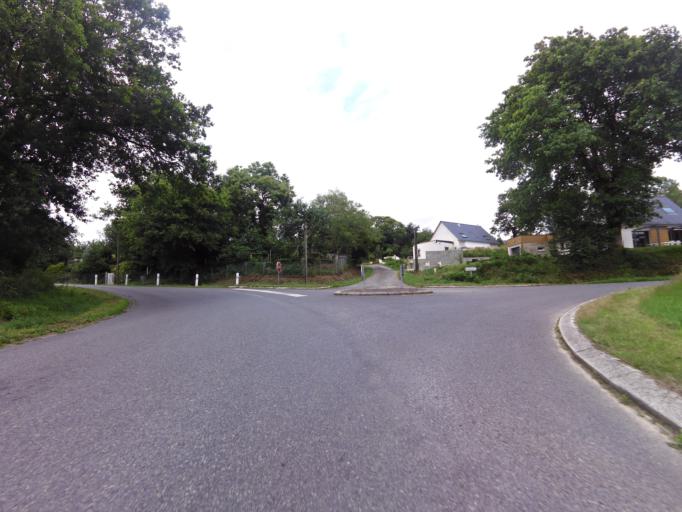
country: FR
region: Brittany
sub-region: Departement du Morbihan
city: Limerzel
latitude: 47.6267
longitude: -2.3967
